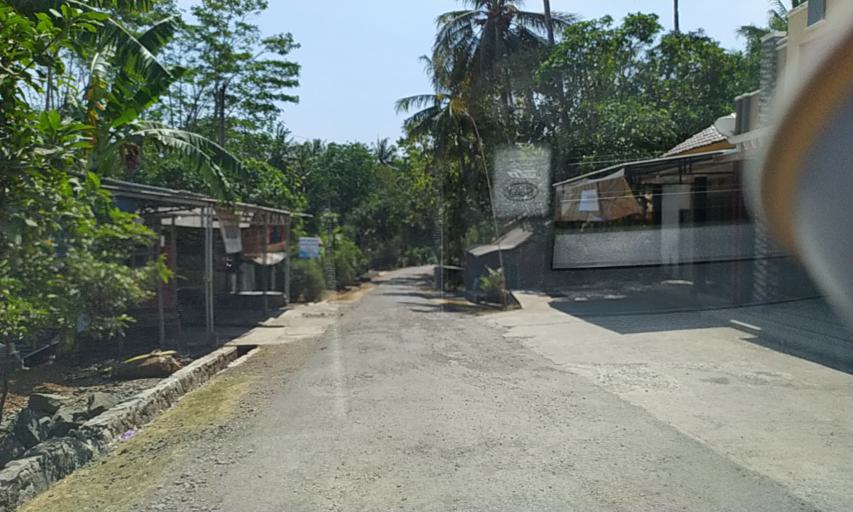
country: ID
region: Central Java
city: Prapagan
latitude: -7.5945
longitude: 108.9958
